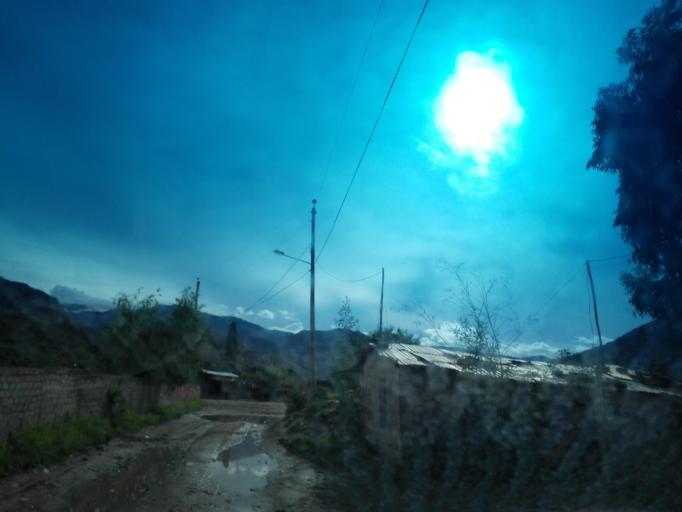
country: PE
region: Ayacucho
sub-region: Provincia de Huamanga
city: Pacaycasa
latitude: -13.0697
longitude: -74.2514
